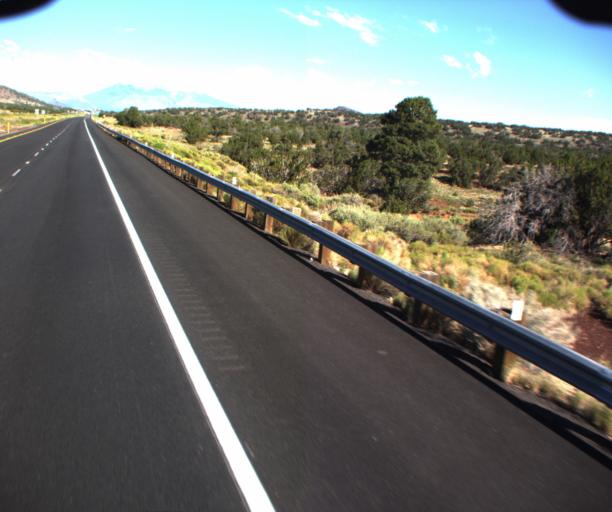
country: US
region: Arizona
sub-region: Coconino County
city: Flagstaff
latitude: 35.1892
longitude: -111.3757
